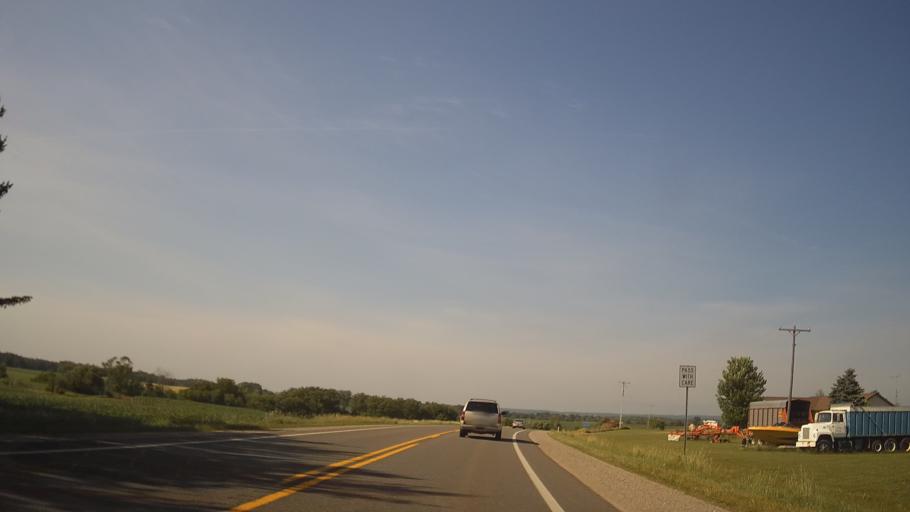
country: US
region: Michigan
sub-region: Ogemaw County
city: West Branch
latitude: 44.3588
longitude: -84.1256
